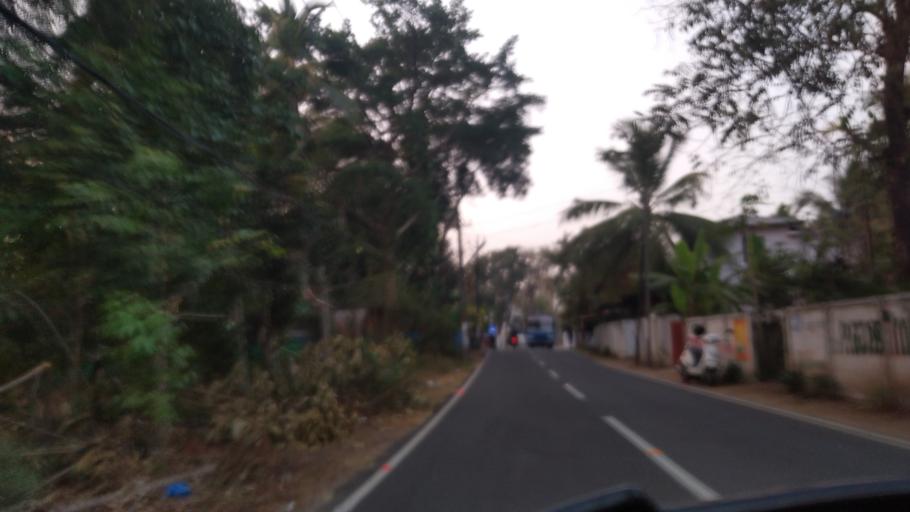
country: IN
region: Kerala
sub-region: Ernakulam
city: Elur
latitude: 10.1242
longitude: 76.2385
